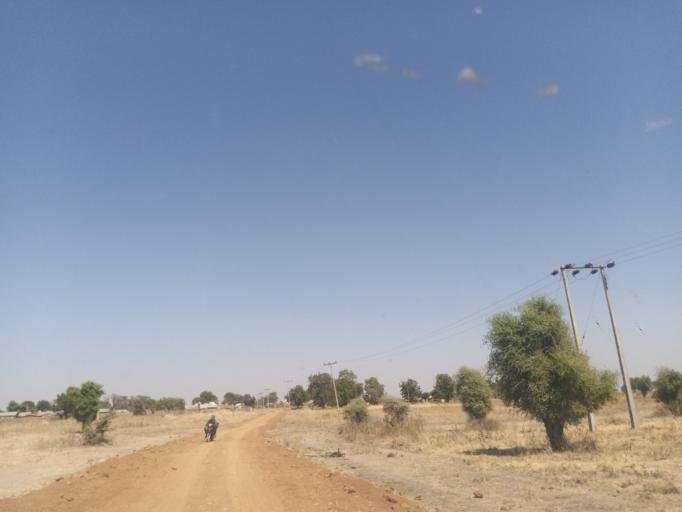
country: NG
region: Adamawa
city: Yola
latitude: 9.3080
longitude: 12.8896
